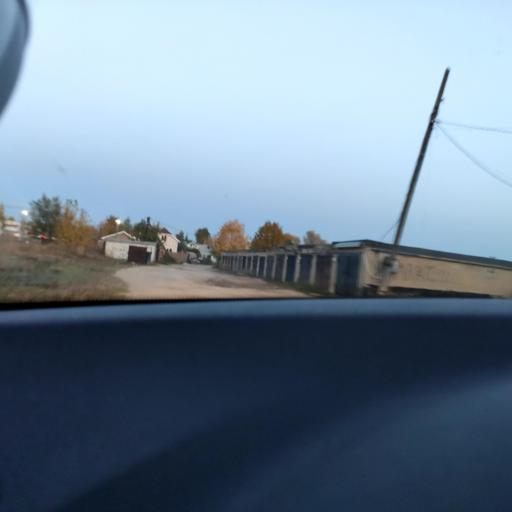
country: RU
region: Samara
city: Novosemeykino
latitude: 53.3690
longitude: 50.3518
